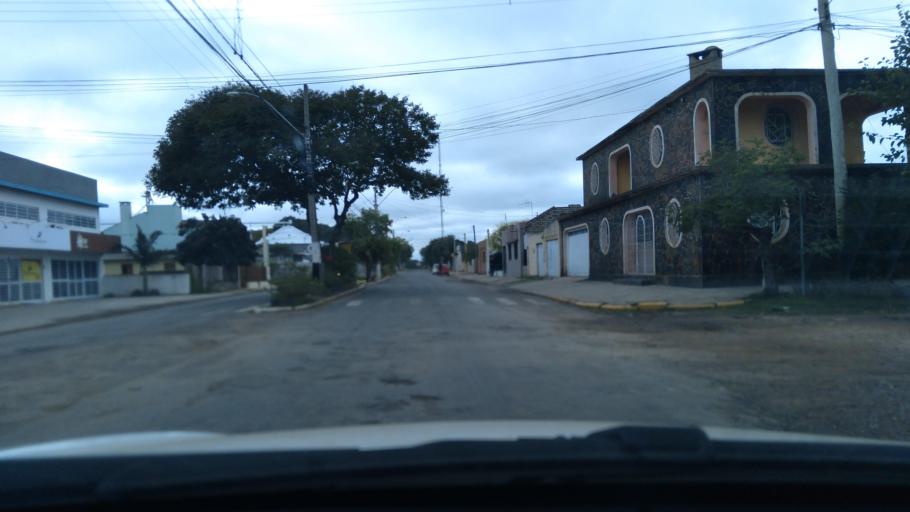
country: BR
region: Rio Grande do Sul
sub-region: Dom Pedrito
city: Dom Pedrito
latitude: -30.9699
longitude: -54.6730
